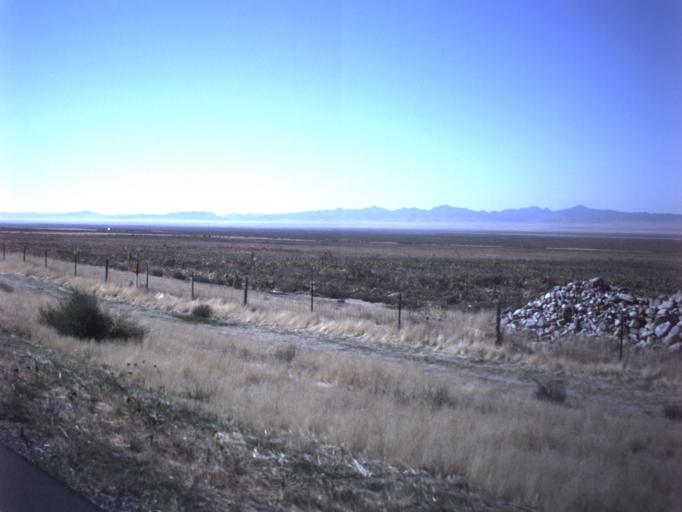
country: US
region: Utah
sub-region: Tooele County
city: Grantsville
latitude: 40.5196
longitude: -112.7477
